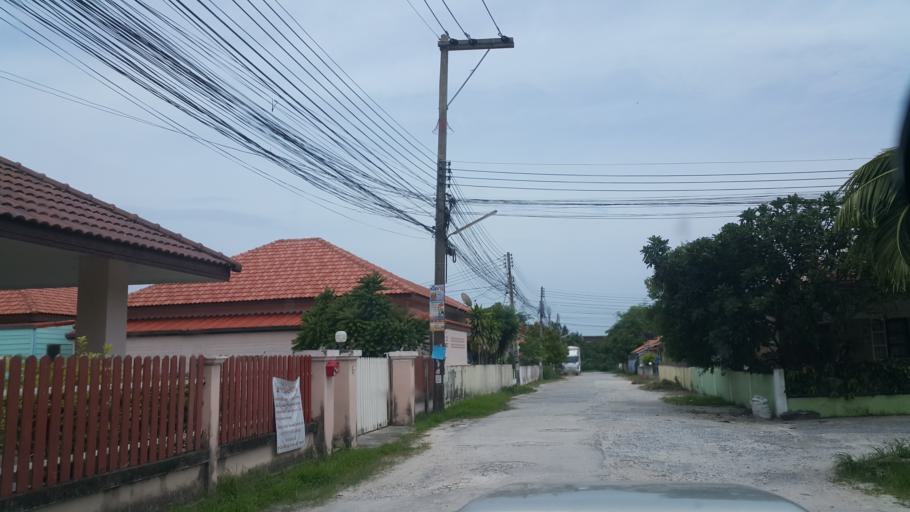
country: TH
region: Rayong
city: Ban Chang
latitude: 12.7179
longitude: 101.0634
